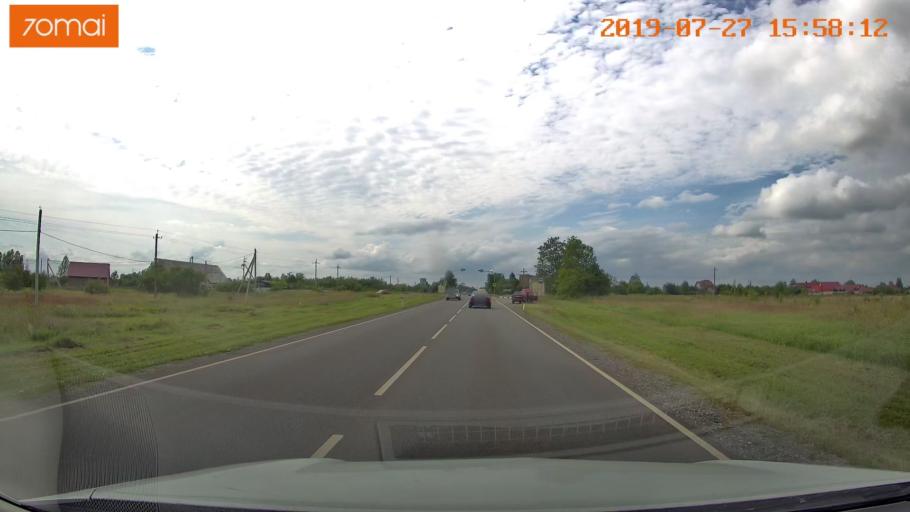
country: RU
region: Kaliningrad
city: Chernyakhovsk
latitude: 54.6257
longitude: 21.8686
